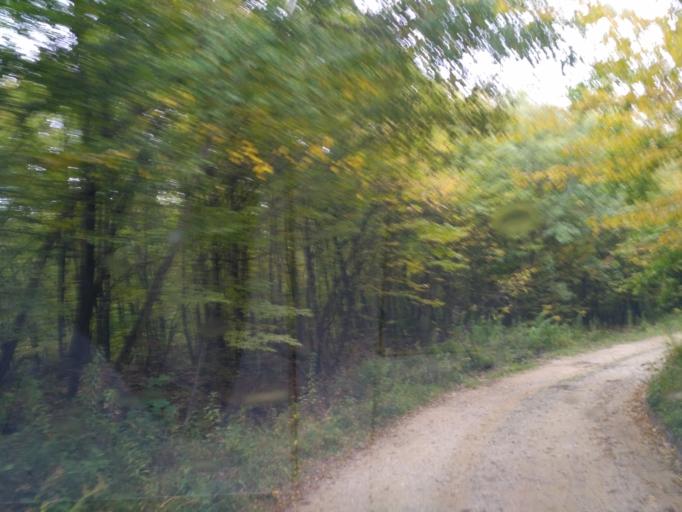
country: SK
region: Kosicky
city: Kosice
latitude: 48.7771
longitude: 21.2797
